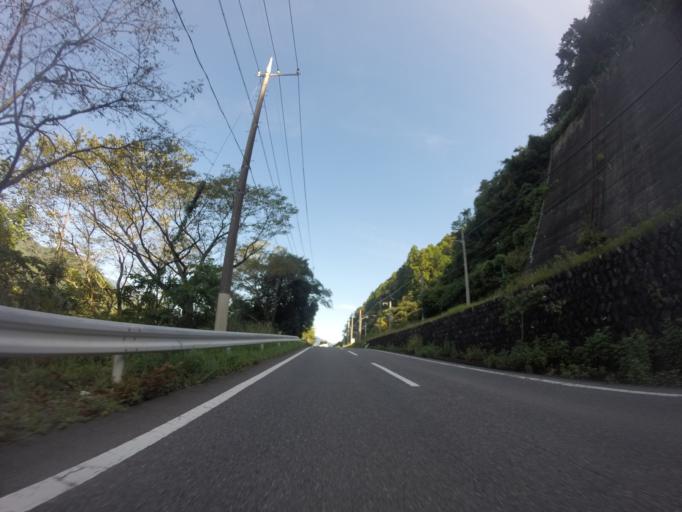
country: JP
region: Shizuoka
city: Fujinomiya
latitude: 35.3047
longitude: 138.4566
